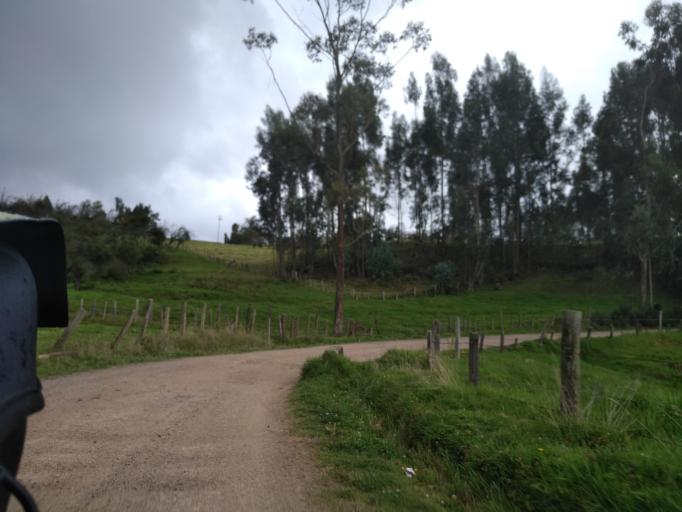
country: CO
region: Boyaca
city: Sotaquira
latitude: 5.7666
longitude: -73.2709
